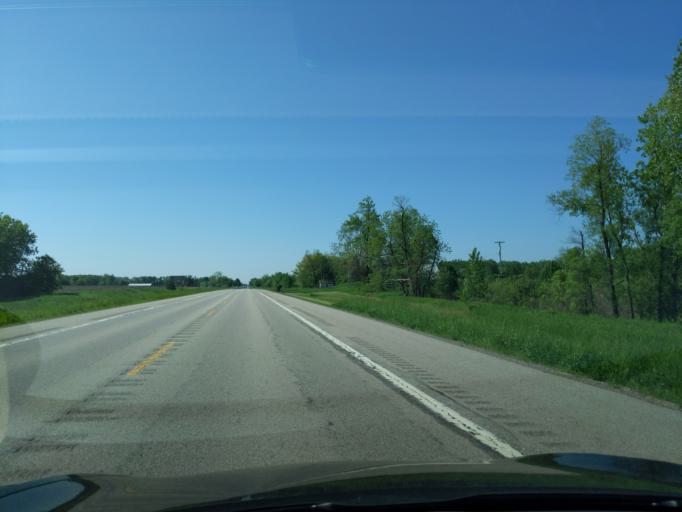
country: US
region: Michigan
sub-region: Ingham County
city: Stockbridge
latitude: 42.5393
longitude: -84.1912
